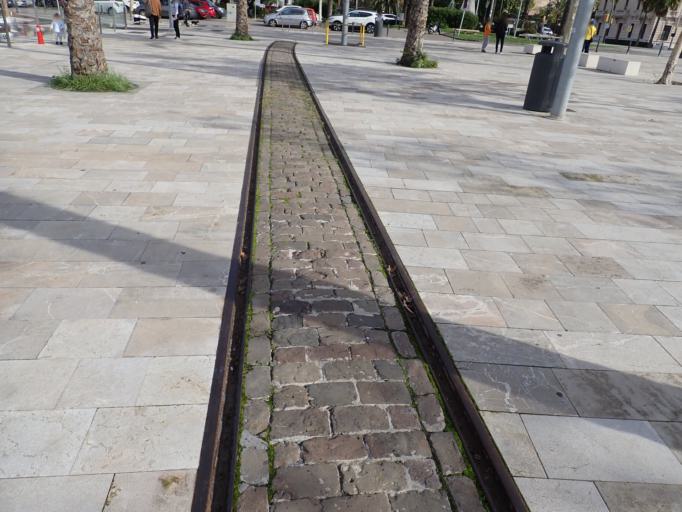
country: ES
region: Balearic Islands
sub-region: Illes Balears
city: Palma
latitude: 39.5669
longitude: 2.6435
